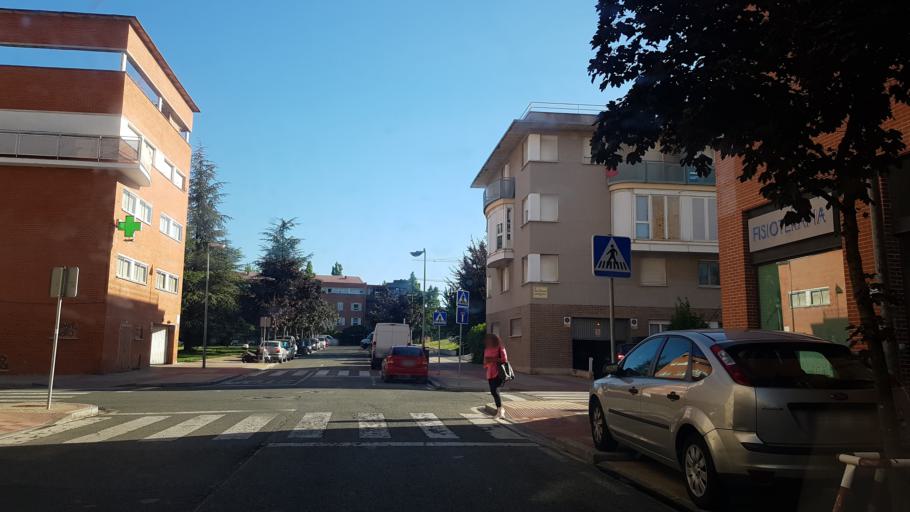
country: ES
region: Navarre
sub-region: Provincia de Navarra
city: Burlata
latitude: 42.8128
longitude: -1.6103
